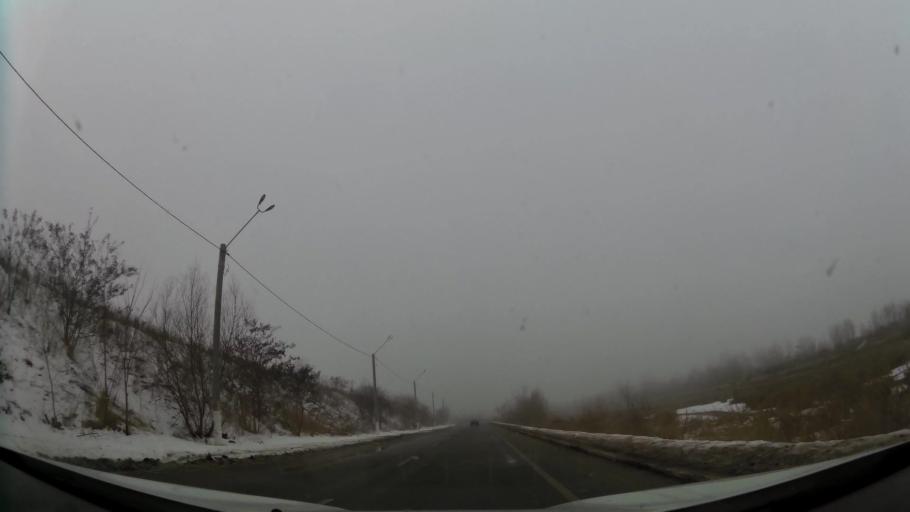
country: RO
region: Ilfov
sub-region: Comuna Chiajna
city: Chiajna
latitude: 44.4654
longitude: 25.9855
